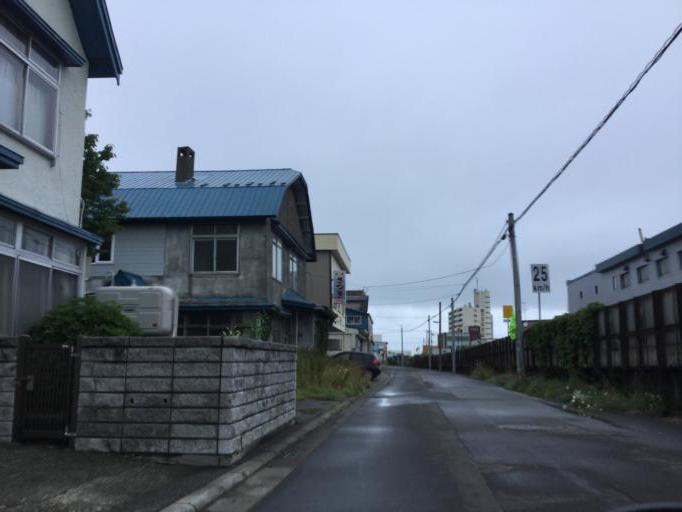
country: JP
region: Hokkaido
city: Wakkanai
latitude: 45.4127
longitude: 141.6767
